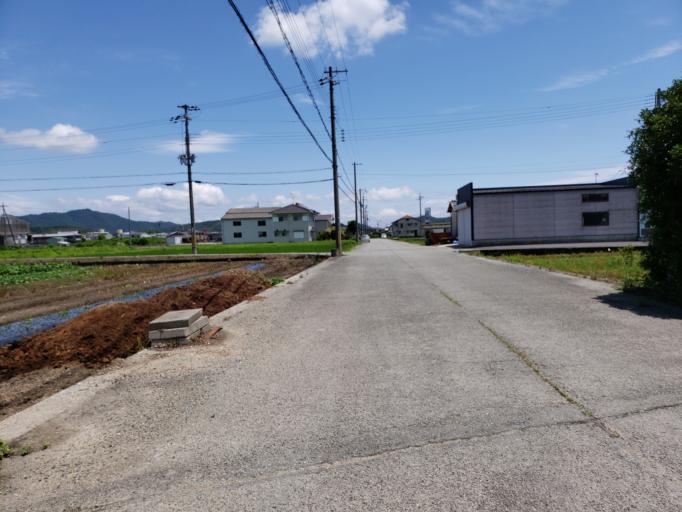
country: JP
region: Hyogo
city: Kakogawacho-honmachi
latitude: 34.8156
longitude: 134.8137
